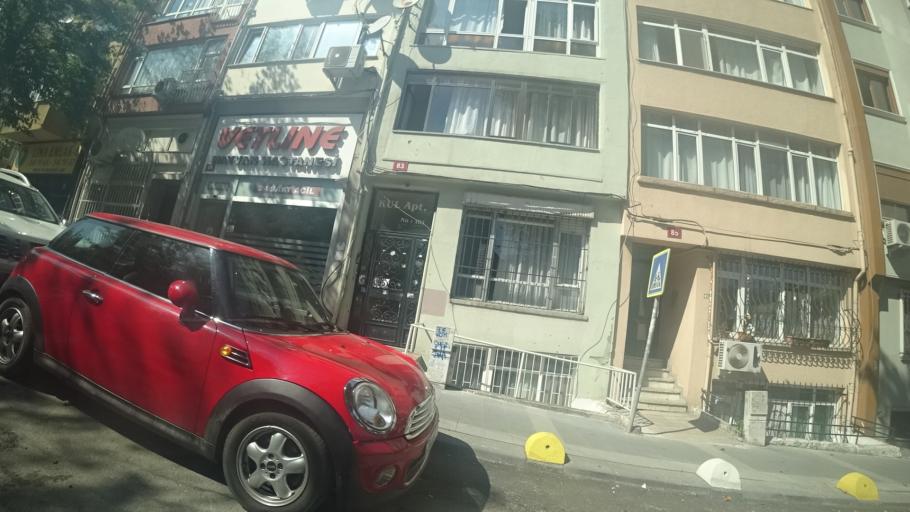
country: TR
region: Istanbul
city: UEskuedar
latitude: 40.9833
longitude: 29.0300
